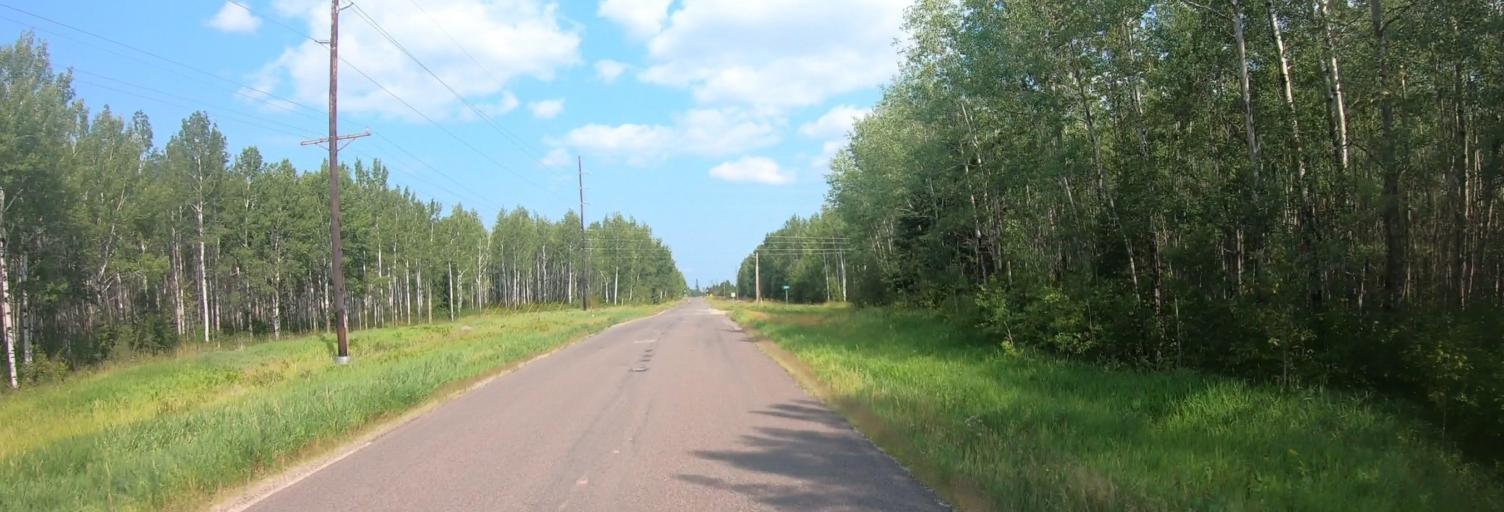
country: US
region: Minnesota
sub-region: Saint Louis County
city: Mountain Iron
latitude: 47.8921
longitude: -92.7198
